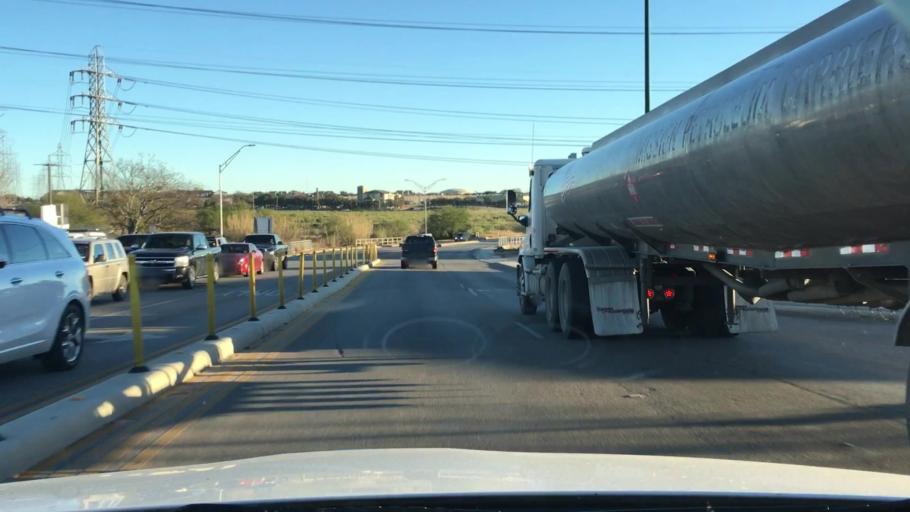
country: US
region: Texas
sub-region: Bexar County
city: Windcrest
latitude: 29.5487
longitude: -98.3755
